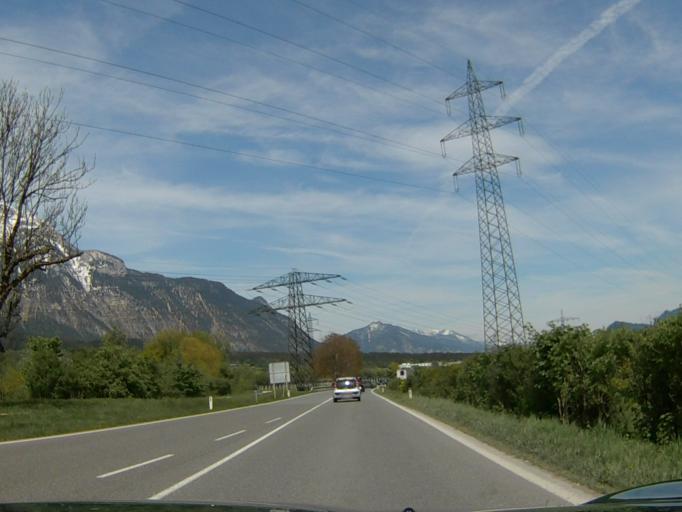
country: AT
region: Tyrol
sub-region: Politischer Bezirk Schwaz
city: Wiesing
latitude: 47.3938
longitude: 11.7988
